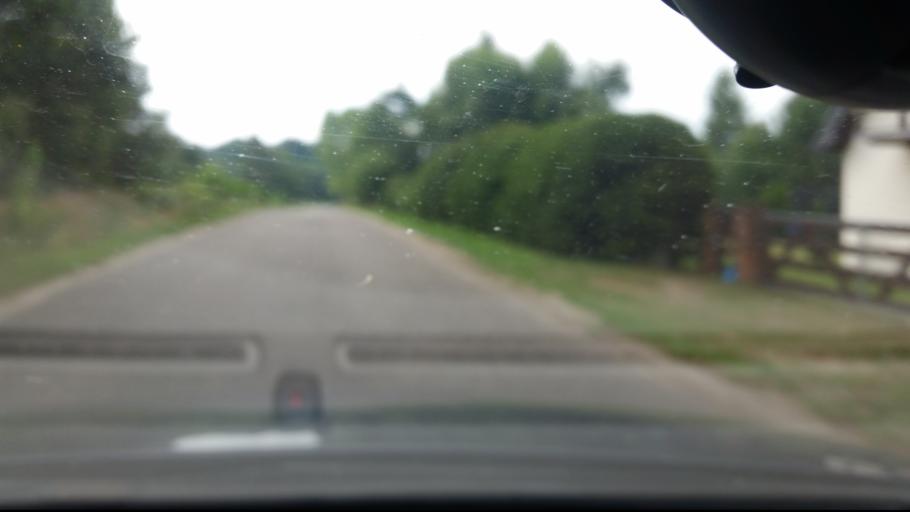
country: PL
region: Pomeranian Voivodeship
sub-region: Powiat wejherowski
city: Choczewo
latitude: 54.7639
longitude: 17.7928
